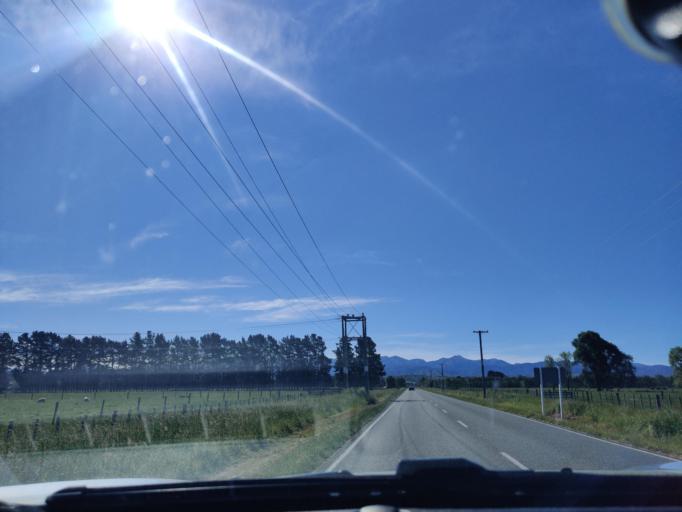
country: NZ
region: Wellington
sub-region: Masterton District
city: Masterton
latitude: -40.9354
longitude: 175.6503
